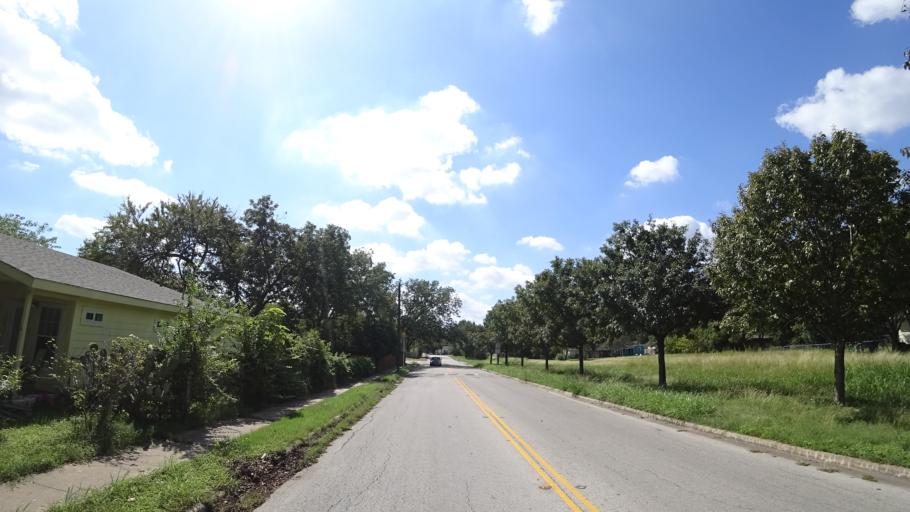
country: US
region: Texas
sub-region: Travis County
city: Austin
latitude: 30.3380
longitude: -97.7110
